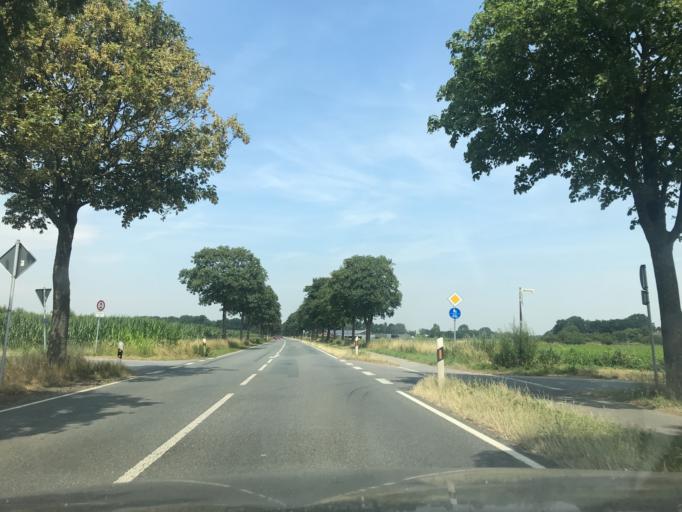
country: DE
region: North Rhine-Westphalia
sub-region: Regierungsbezirk Dusseldorf
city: Issum
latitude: 51.5088
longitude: 6.4205
